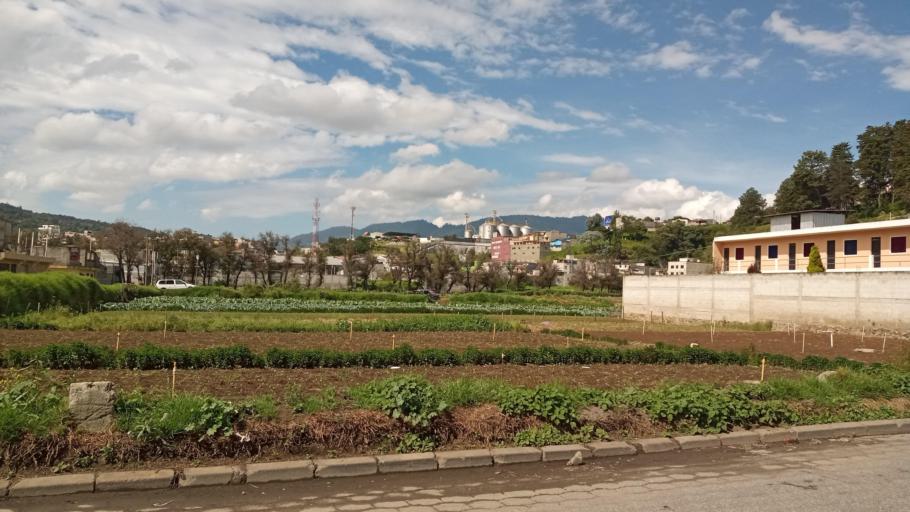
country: GT
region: Quetzaltenango
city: Quetzaltenango
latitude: 14.8442
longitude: -91.5088
